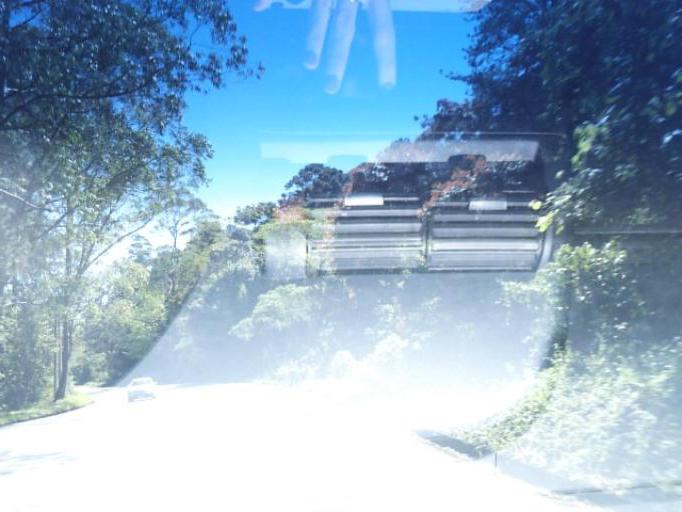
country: BR
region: Sao Paulo
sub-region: Campos Do Jordao
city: Campos do Jordao
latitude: -22.8172
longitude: -45.6265
